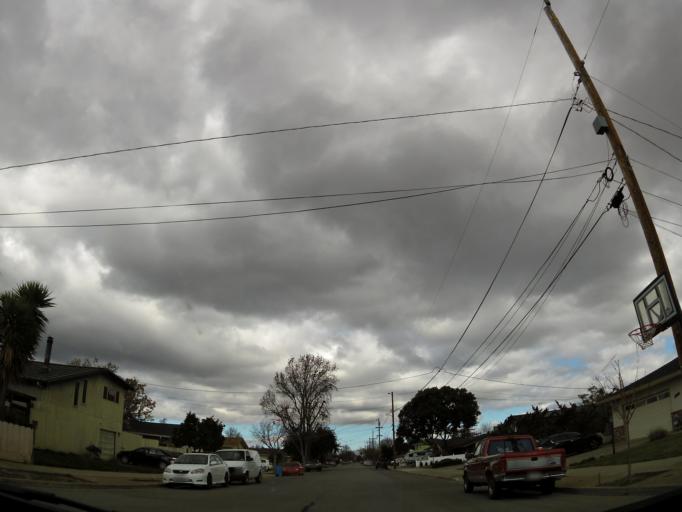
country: US
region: California
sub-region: San Benito County
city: Hollister
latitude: 36.8341
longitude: -121.3995
